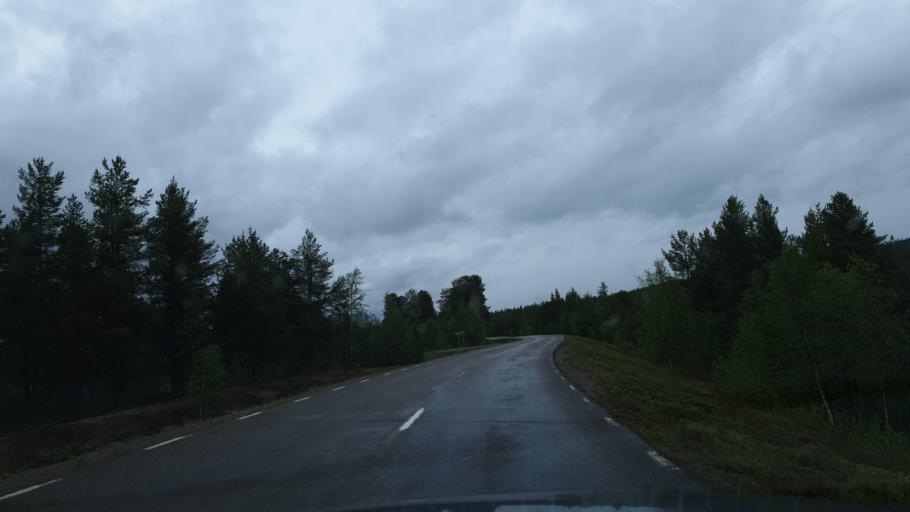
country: SE
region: Norrbotten
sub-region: Kiruna Kommun
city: Kiruna
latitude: 67.8642
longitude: 20.9801
